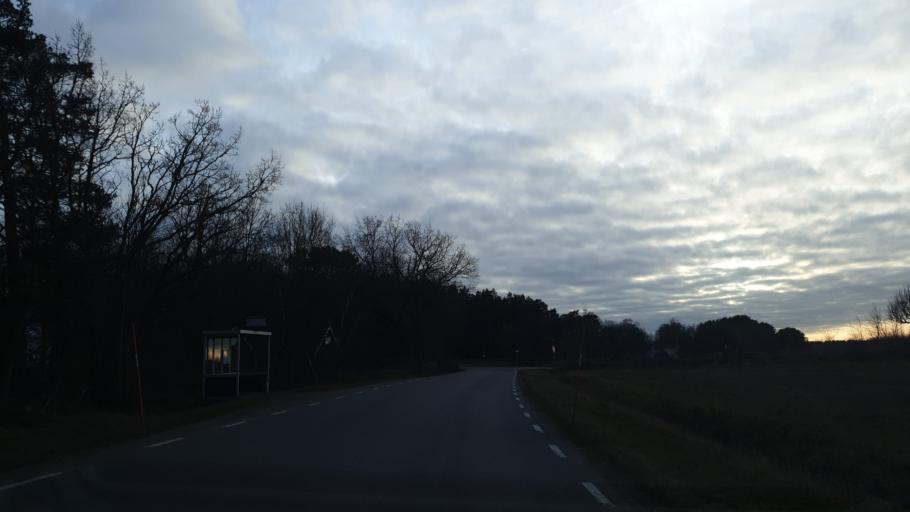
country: SE
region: Kalmar
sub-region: Torsas Kommun
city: Torsas
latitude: 56.2334
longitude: 15.9977
